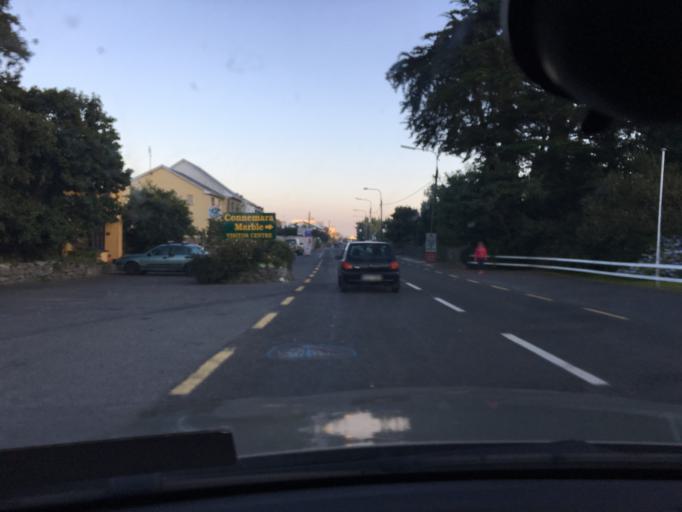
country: IE
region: Connaught
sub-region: County Galway
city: Moycullen
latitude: 53.3408
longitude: -9.1845
